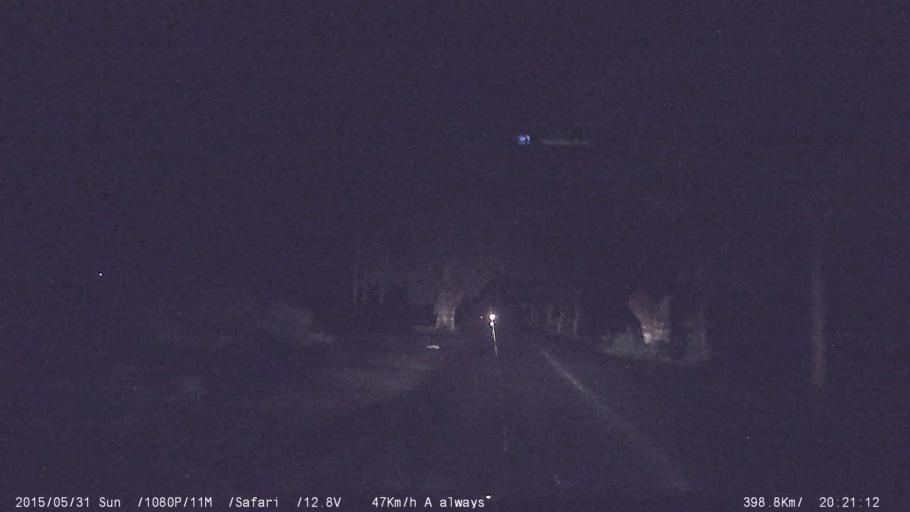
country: IN
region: Karnataka
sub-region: Mandya
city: Malavalli
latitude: 12.4213
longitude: 77.2115
